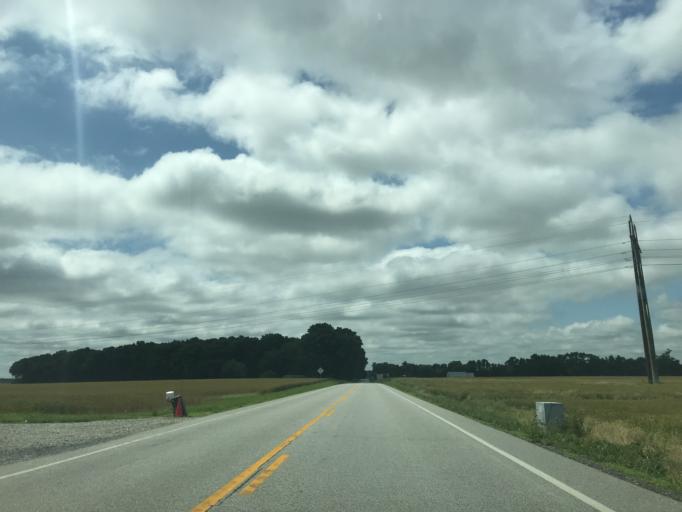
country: US
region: Maryland
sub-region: Caroline County
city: Ridgely
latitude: 38.9269
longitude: -75.8936
